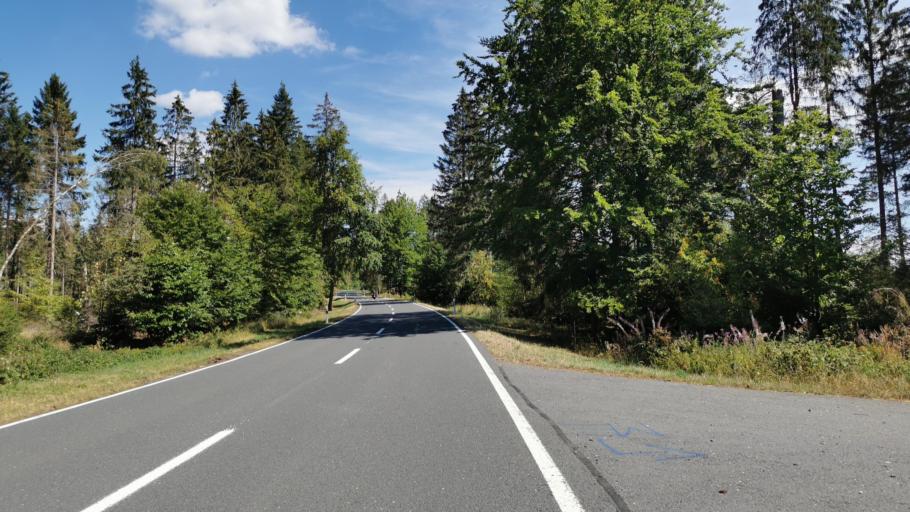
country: DE
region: Bavaria
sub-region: Upper Franconia
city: Nordhalben
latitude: 50.4010
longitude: 11.5144
